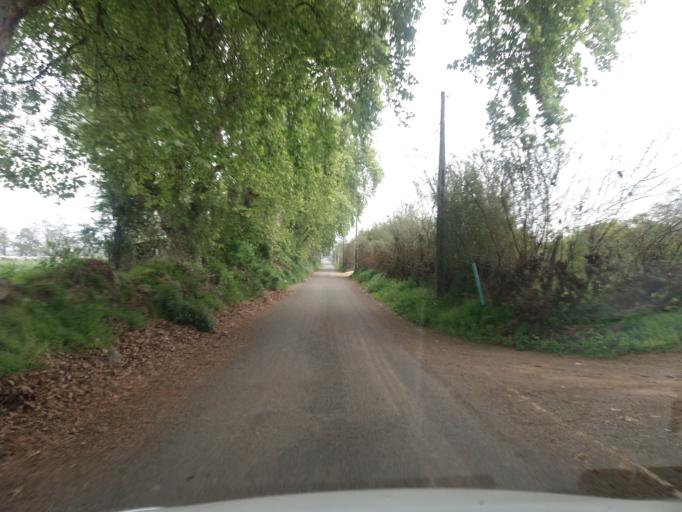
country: CL
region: Valparaiso
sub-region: Provincia de San Felipe
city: Llaillay
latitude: -32.8488
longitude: -71.0615
